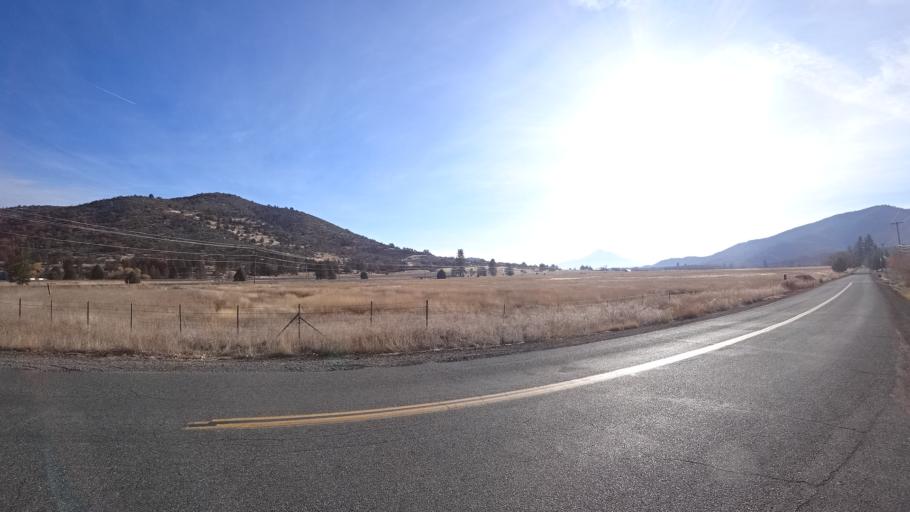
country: US
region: California
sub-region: Siskiyou County
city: Yreka
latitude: 41.6817
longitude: -122.6351
